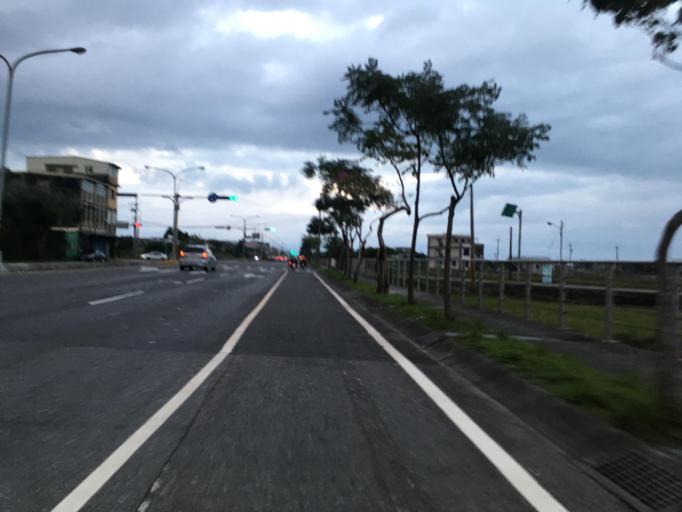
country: TW
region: Taiwan
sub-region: Yilan
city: Yilan
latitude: 24.6187
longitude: 121.8444
